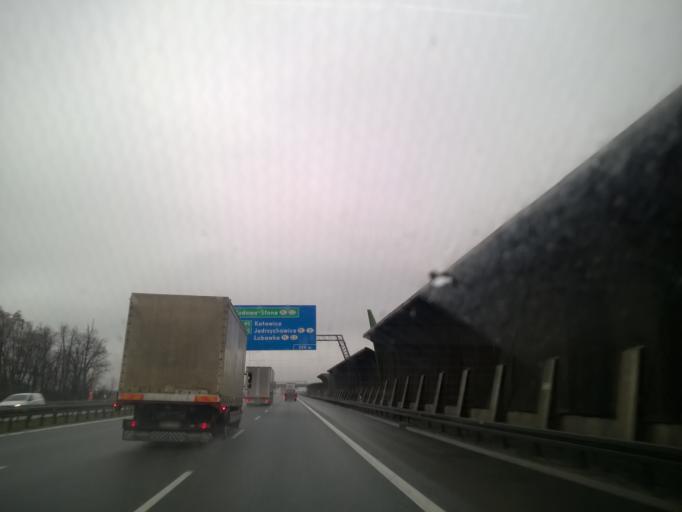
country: PL
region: Lower Silesian Voivodeship
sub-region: Powiat wroclawski
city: Tyniec Maly
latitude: 51.0581
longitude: 16.9309
